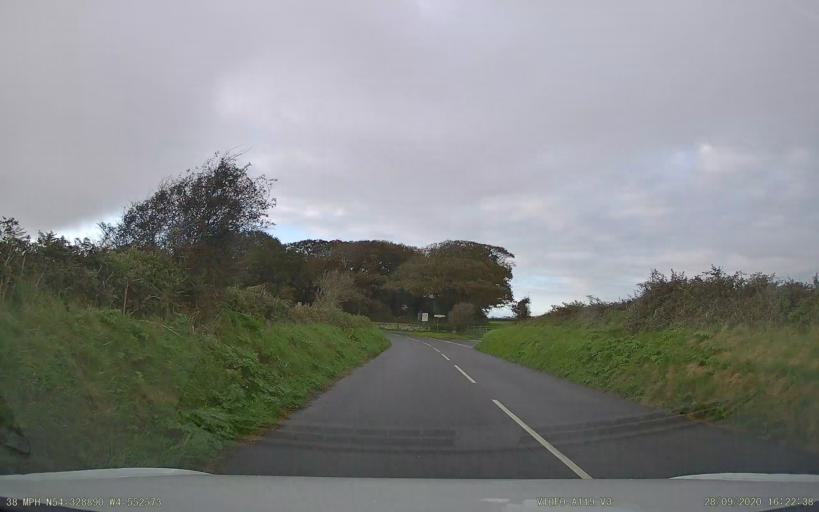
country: IM
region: Ramsey
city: Ramsey
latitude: 54.3289
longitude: -4.5526
